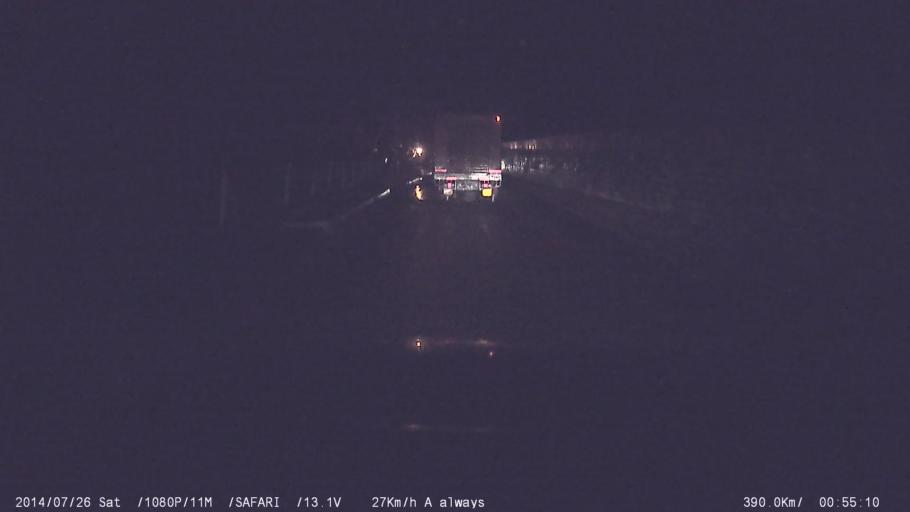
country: IN
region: Kerala
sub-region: Palakkad district
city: Palakkad
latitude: 10.7928
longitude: 76.7299
